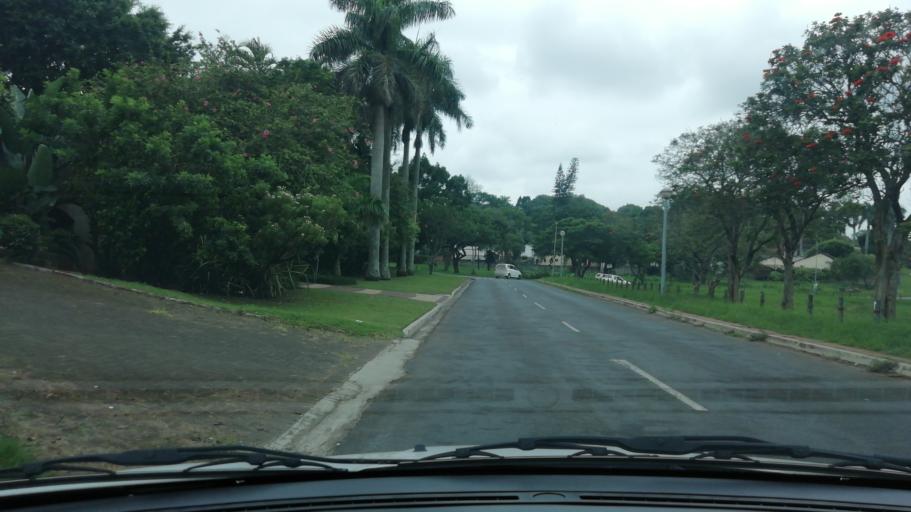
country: ZA
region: KwaZulu-Natal
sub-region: uThungulu District Municipality
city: Empangeni
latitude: -28.7577
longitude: 31.8907
